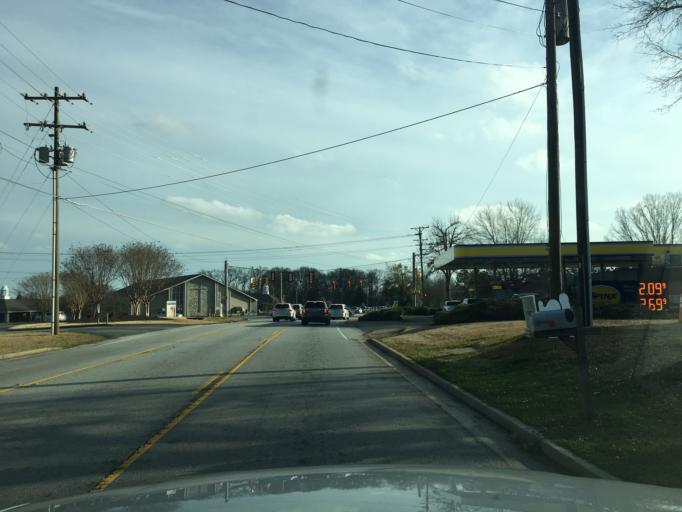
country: US
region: South Carolina
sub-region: Greenville County
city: Taylors
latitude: 34.8933
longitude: -82.2900
